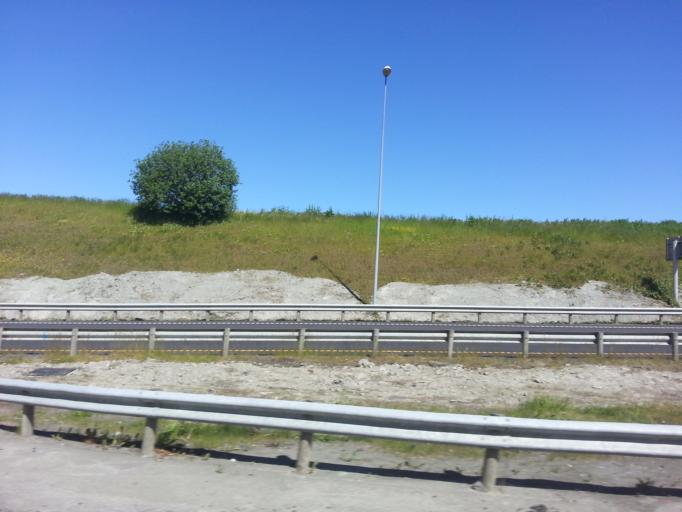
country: NO
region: Sor-Trondelag
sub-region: Trondheim
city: Trondheim
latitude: 63.4268
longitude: 10.5112
